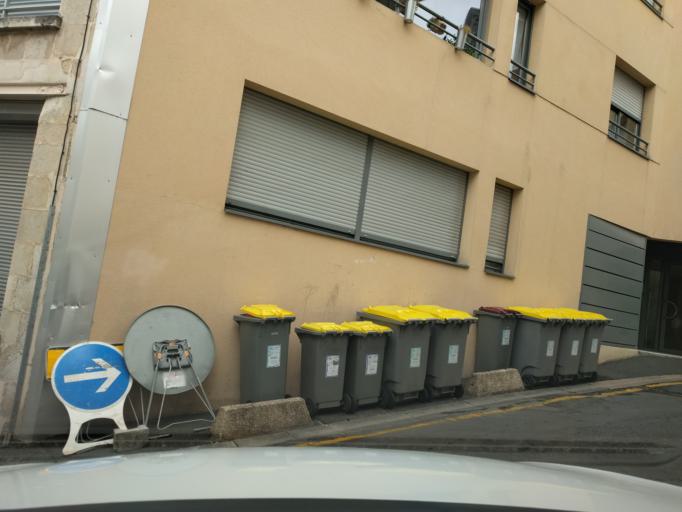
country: FR
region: Poitou-Charentes
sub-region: Departement des Deux-Sevres
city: Niort
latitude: 46.3257
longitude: -0.4623
